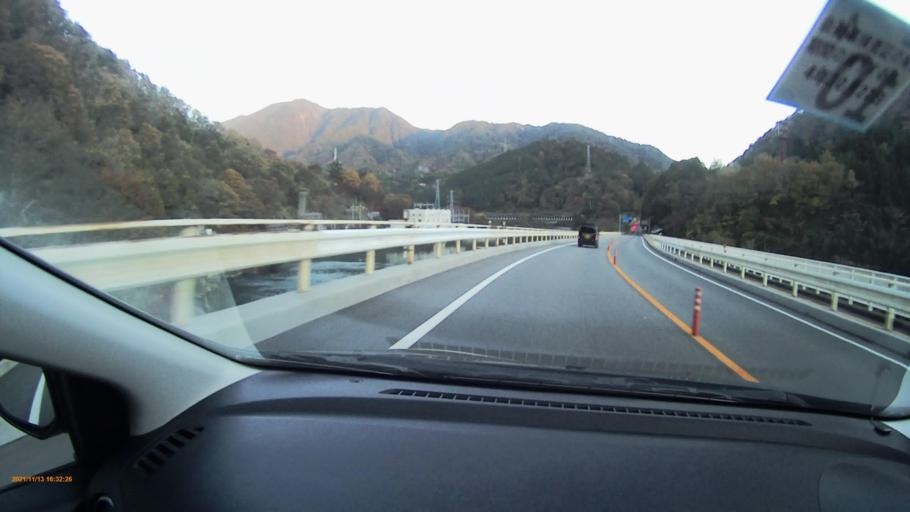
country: JP
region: Gifu
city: Nakatsugawa
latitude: 35.5891
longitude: 137.5883
